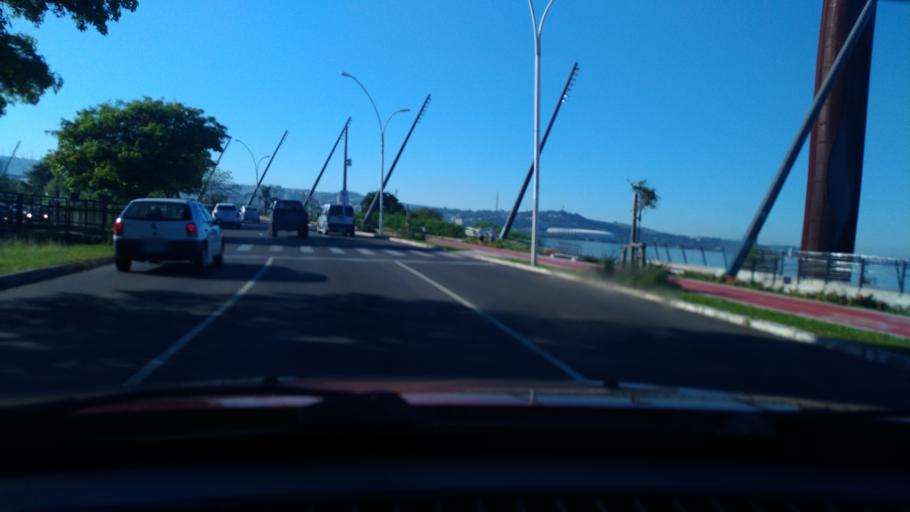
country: BR
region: Rio Grande do Sul
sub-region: Porto Alegre
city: Porto Alegre
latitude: -30.0411
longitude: -51.2409
